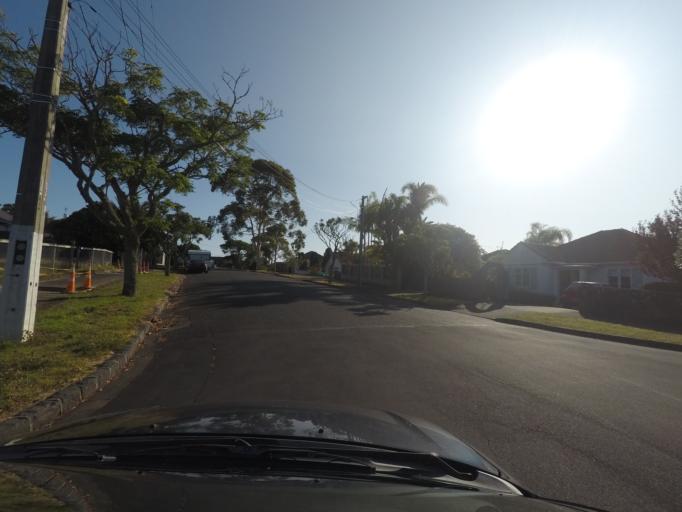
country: NZ
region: Auckland
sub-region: Auckland
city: Rosebank
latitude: -36.8633
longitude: 174.7133
